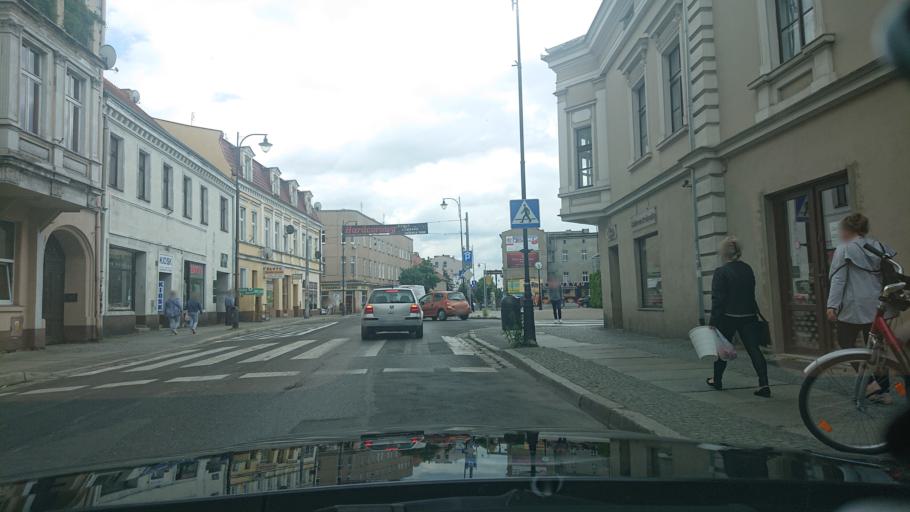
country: PL
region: Greater Poland Voivodeship
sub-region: Powiat gnieznienski
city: Gniezno
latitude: 52.5332
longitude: 17.5963
